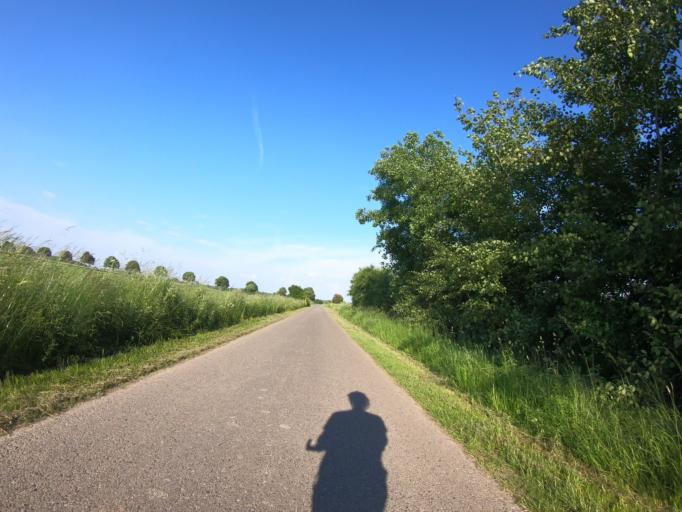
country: DE
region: Lower Saxony
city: Meine
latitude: 52.3639
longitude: 10.5478
